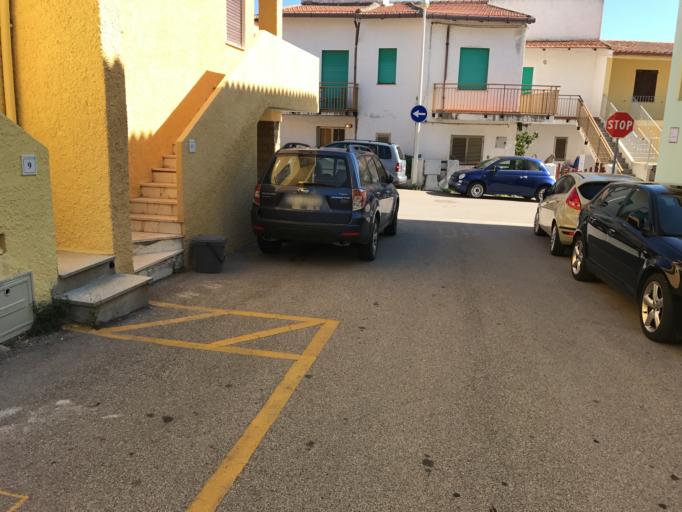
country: IT
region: Sardinia
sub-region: Provincia di Olbia-Tempio
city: Trinita d'Agultu
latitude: 41.0125
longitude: 8.8773
